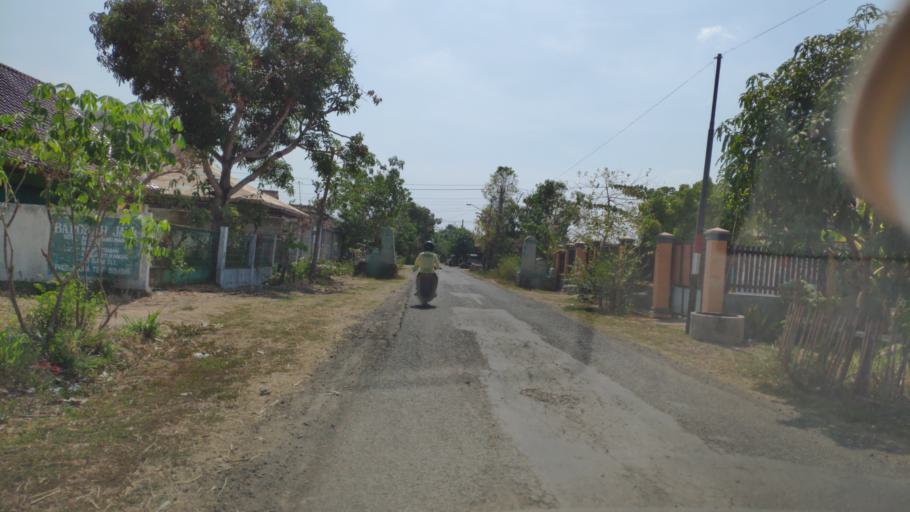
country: ID
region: Central Java
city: Bangkle
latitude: -6.9817
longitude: 111.4357
